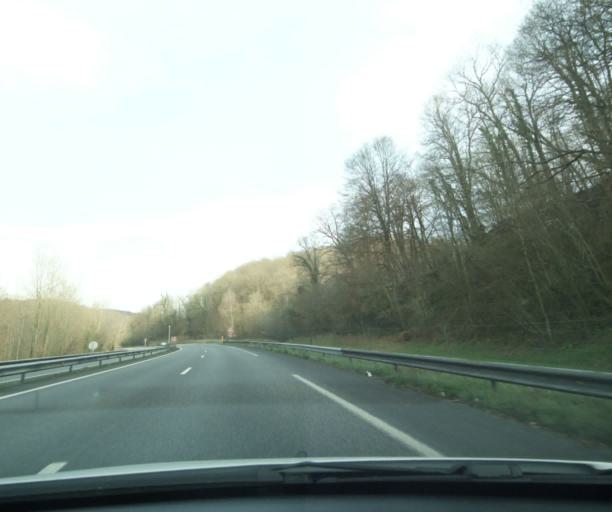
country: FR
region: Midi-Pyrenees
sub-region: Departement des Hautes-Pyrenees
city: Tournay
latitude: 43.1614
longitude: 0.2746
